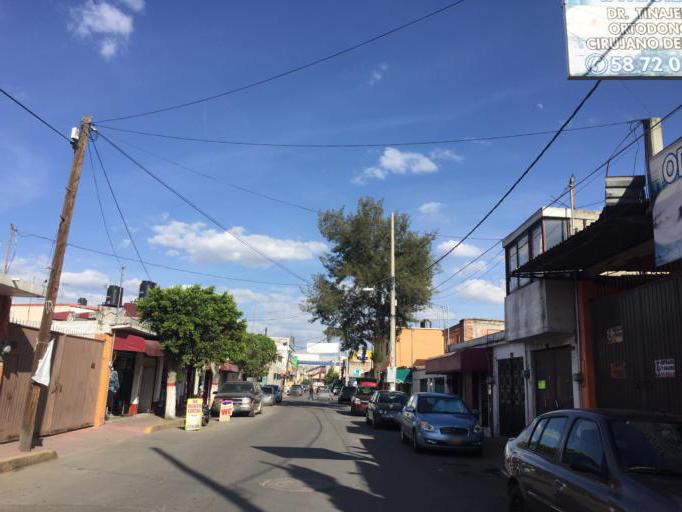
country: MX
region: Mexico
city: Cuautitlan
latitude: 19.6672
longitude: -99.1797
